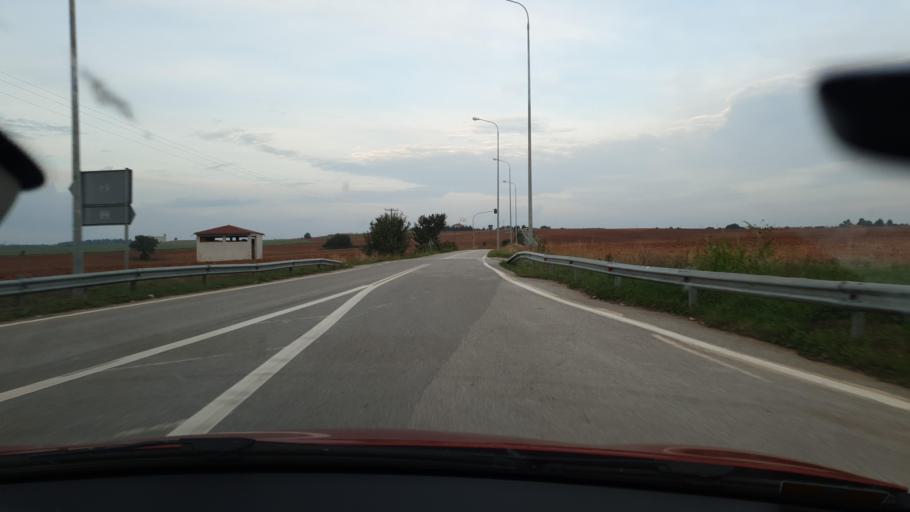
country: GR
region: Central Macedonia
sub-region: Nomos Kilkis
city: Kristoni
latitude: 40.9531
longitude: 22.8309
